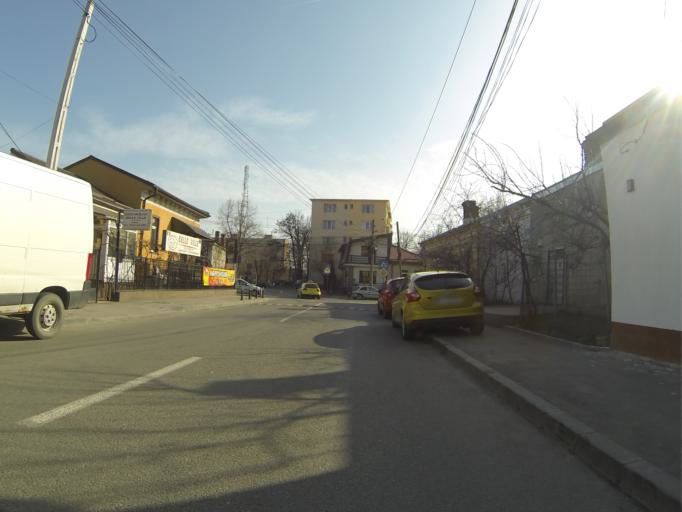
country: RO
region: Dolj
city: Craiova
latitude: 44.3197
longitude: 23.8154
